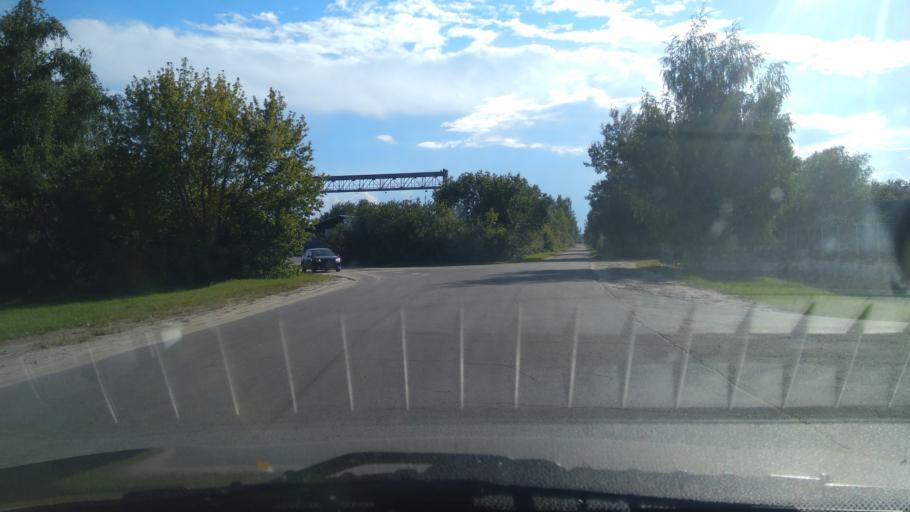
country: BY
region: Brest
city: Byelaazyorsk
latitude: 52.4584
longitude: 25.1890
